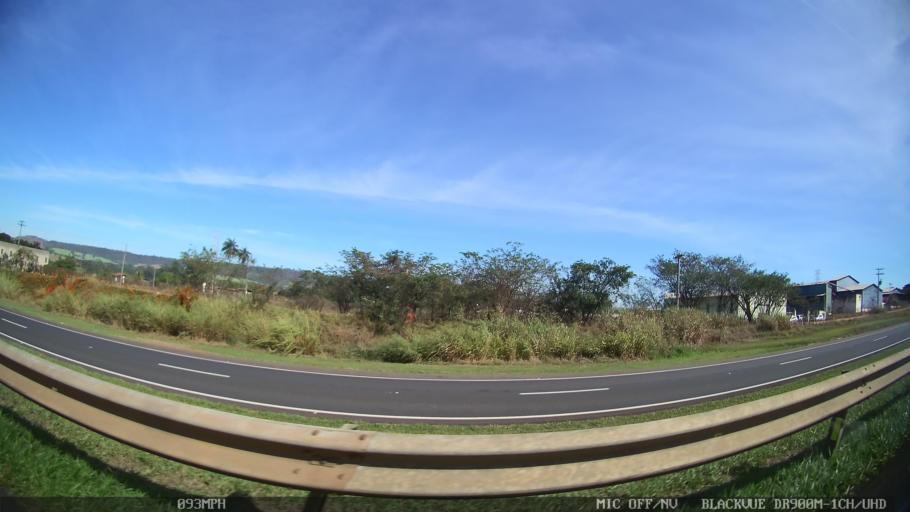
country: BR
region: Sao Paulo
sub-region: Pirassununga
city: Pirassununga
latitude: -21.9883
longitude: -47.4491
